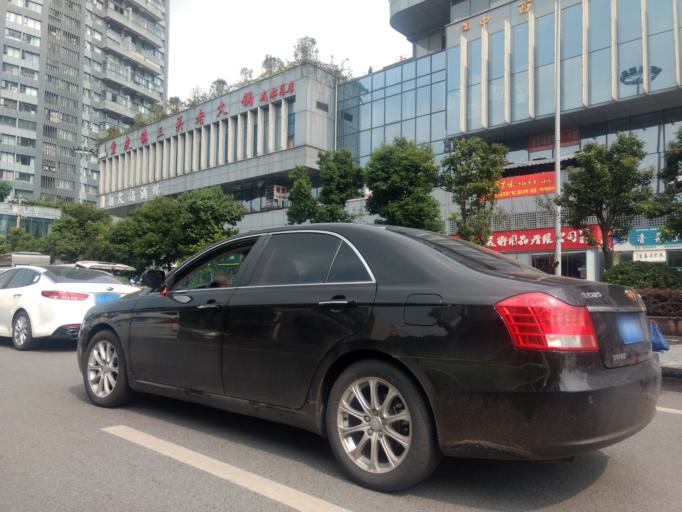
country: CN
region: Sichuan
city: Chengdu
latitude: 30.6621
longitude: 104.0372
